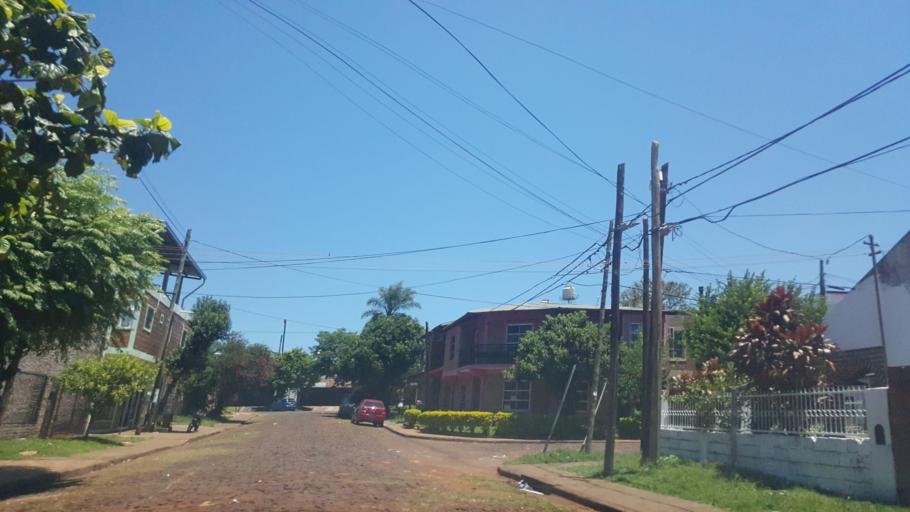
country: AR
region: Misiones
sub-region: Departamento de Capital
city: Posadas
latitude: -27.3851
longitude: -55.9163
